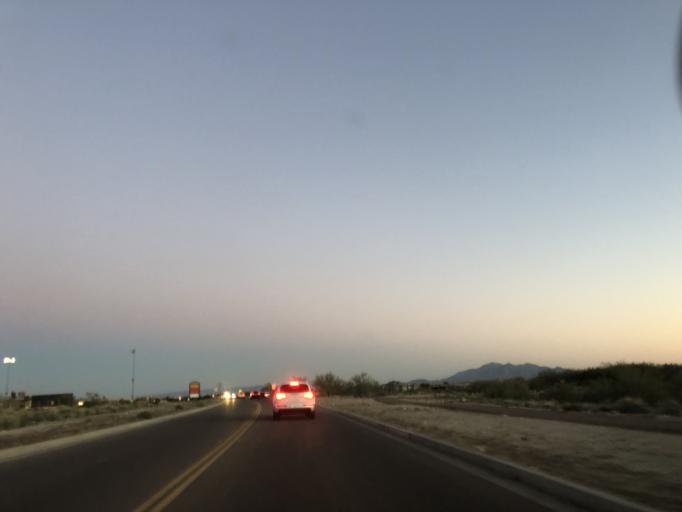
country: US
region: Arizona
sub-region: Maricopa County
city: Citrus Park
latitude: 33.4949
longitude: -112.4984
